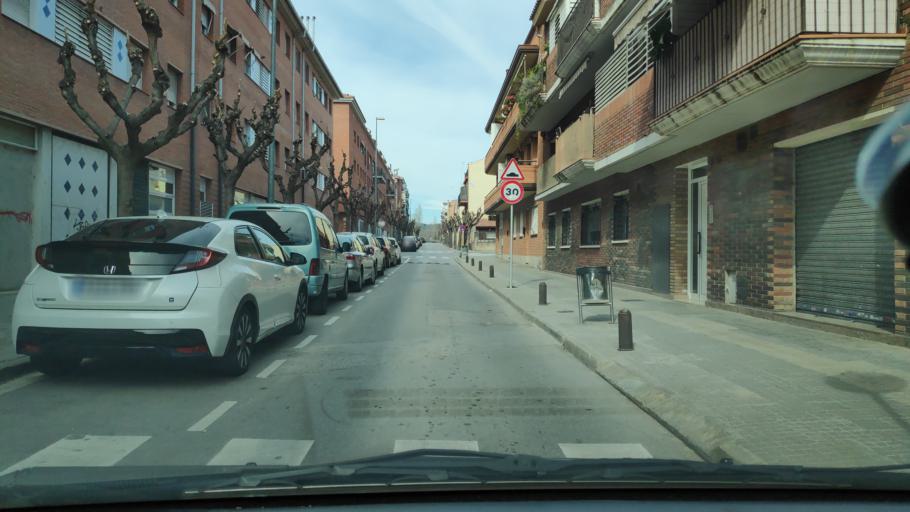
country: ES
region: Catalonia
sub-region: Provincia de Barcelona
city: Rubi
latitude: 41.4949
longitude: 2.0303
